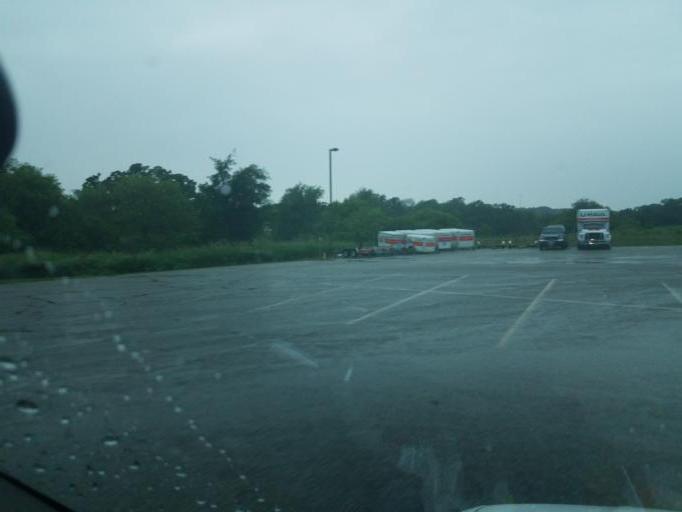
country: US
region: Wisconsin
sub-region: Vernon County
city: Hillsboro
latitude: 43.6610
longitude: -90.3281
